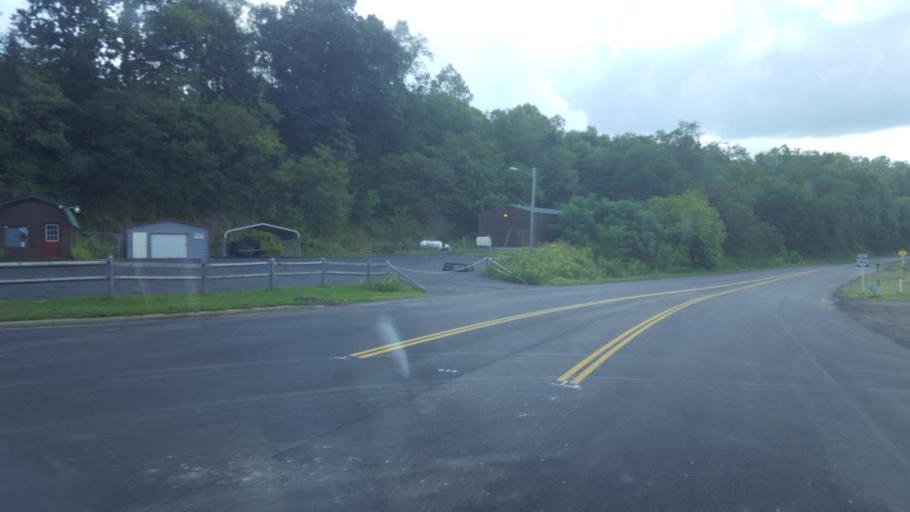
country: US
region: Ohio
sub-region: Columbiana County
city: Lisbon
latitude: 40.7652
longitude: -80.7129
